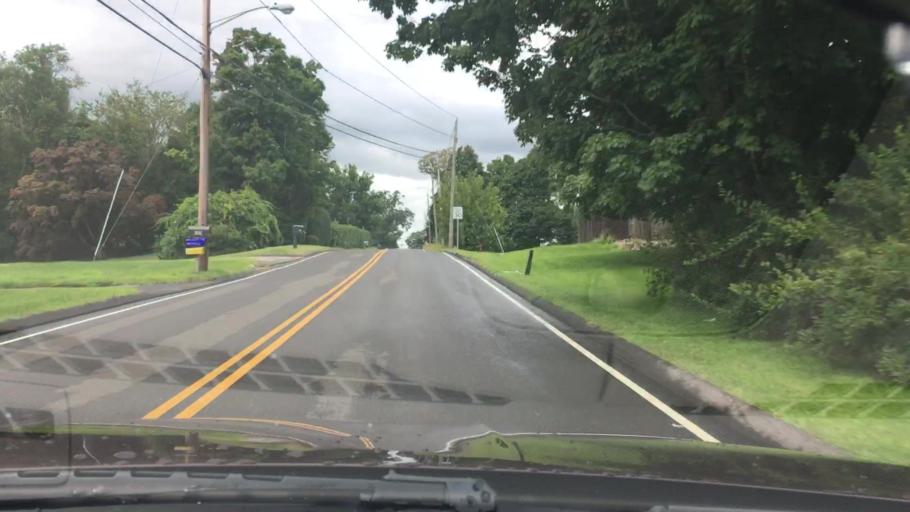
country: US
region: Connecticut
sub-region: Hartford County
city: Manchester
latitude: 41.7391
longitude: -72.5368
